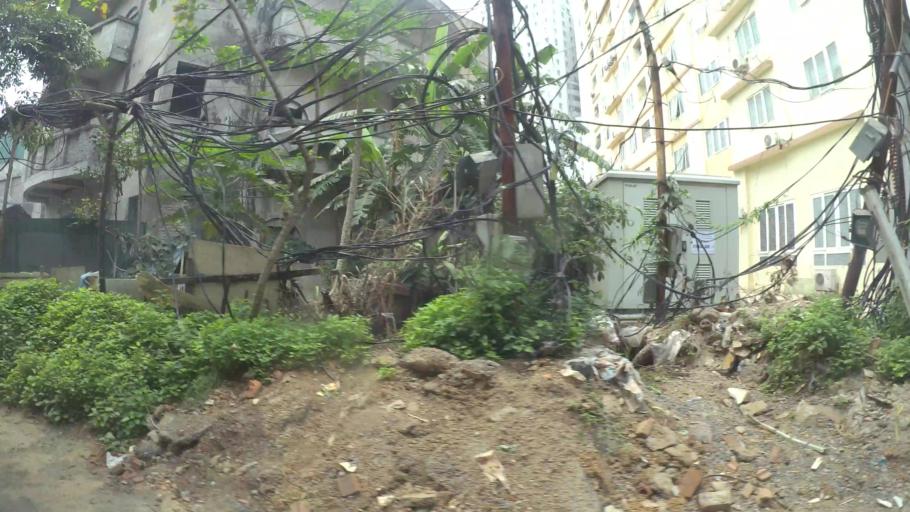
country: VN
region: Ha Noi
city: Ha Dong
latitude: 20.9736
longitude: 105.7644
